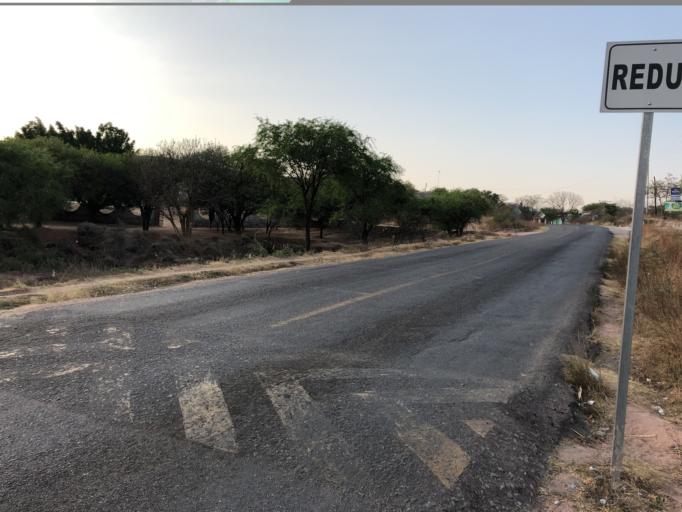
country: MX
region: Oaxaca
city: Ciudad de Huajuapam de Leon
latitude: 17.8396
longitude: -97.7921
